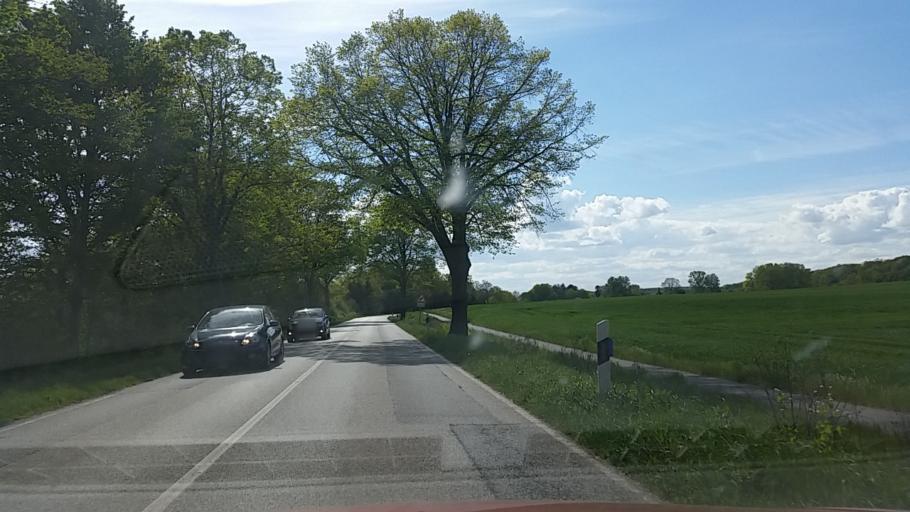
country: DE
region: Schleswig-Holstein
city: Meddewade
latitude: 53.8208
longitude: 10.4682
